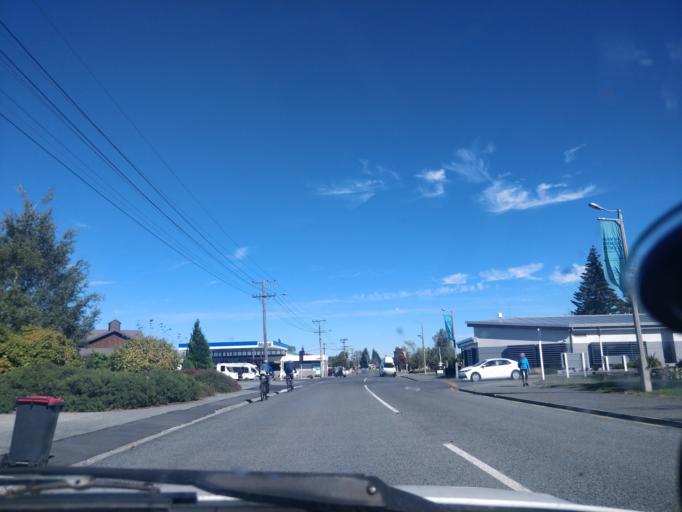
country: NZ
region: Canterbury
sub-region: Timaru District
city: Pleasant Point
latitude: -44.2571
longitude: 170.1006
